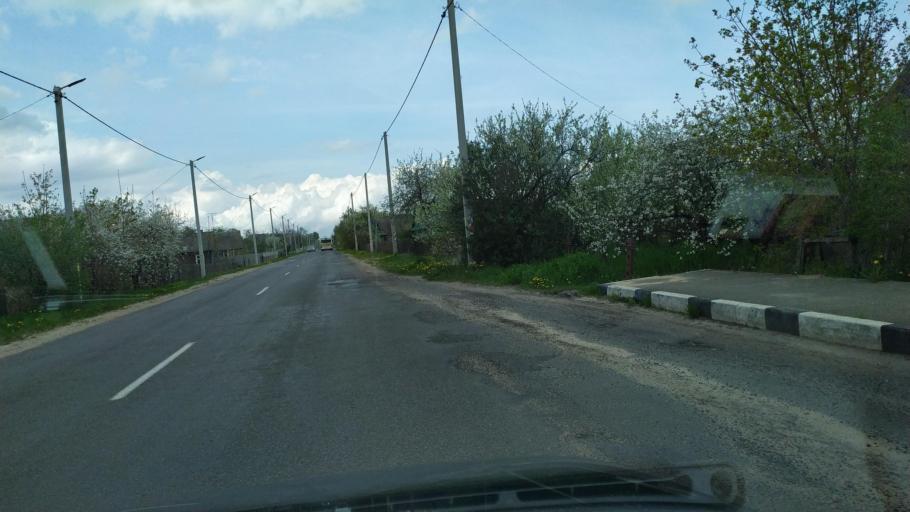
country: BY
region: Brest
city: Pruzhany
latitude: 52.5777
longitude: 24.4126
